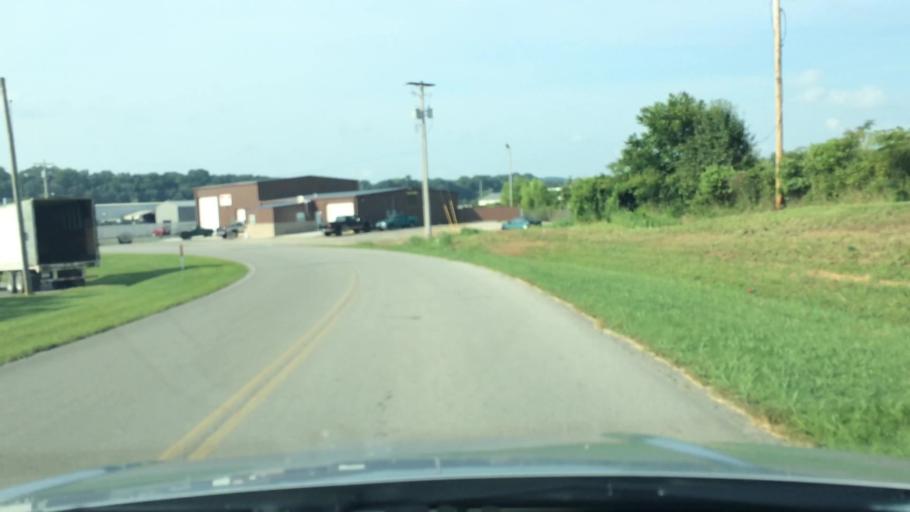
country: US
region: Tennessee
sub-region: Loudon County
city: Lenoir City
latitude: 35.7874
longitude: -84.2667
